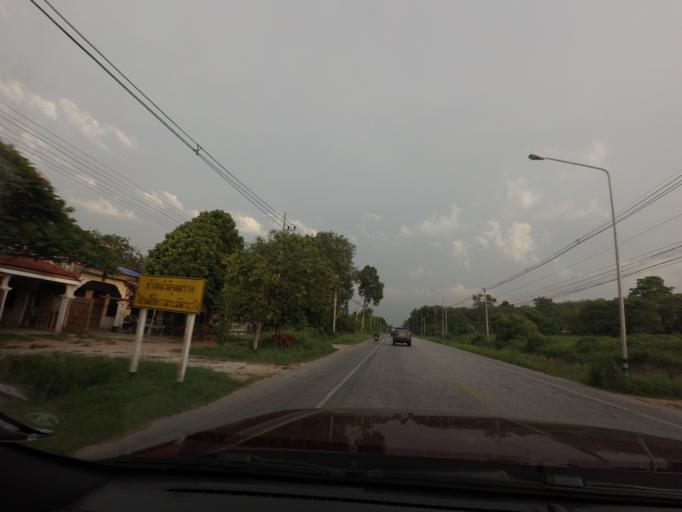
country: TH
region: Pattani
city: Mae Lan
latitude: 6.6043
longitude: 101.1930
